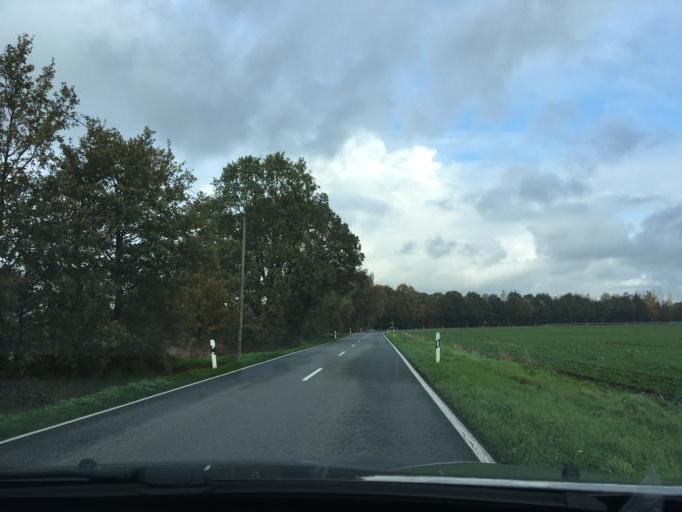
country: NL
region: Gelderland
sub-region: Berkelland
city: Eibergen
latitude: 52.0640
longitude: 6.7068
